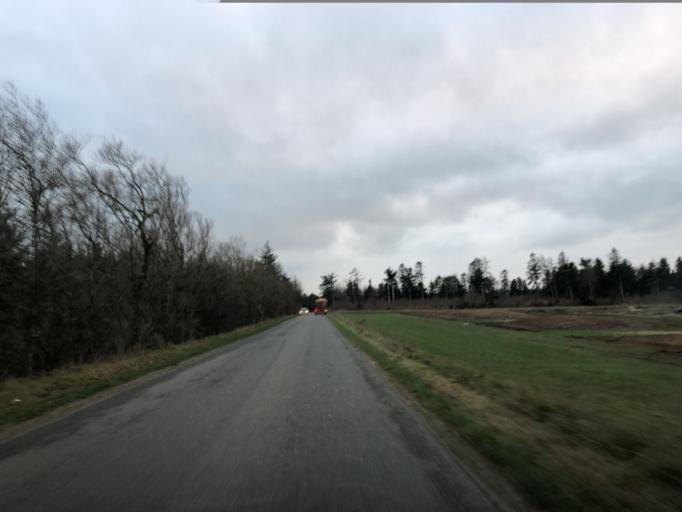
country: DK
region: Central Jutland
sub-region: Holstebro Kommune
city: Ulfborg
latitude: 56.2547
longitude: 8.2820
